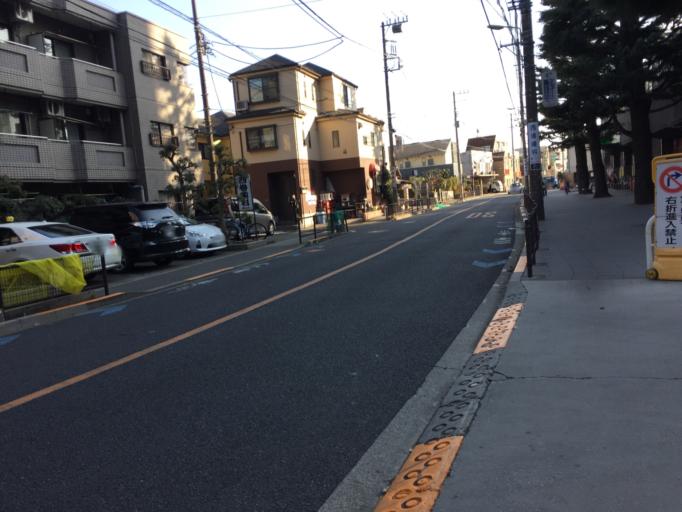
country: JP
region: Tokyo
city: Mitaka-shi
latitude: 35.6572
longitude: 139.6093
